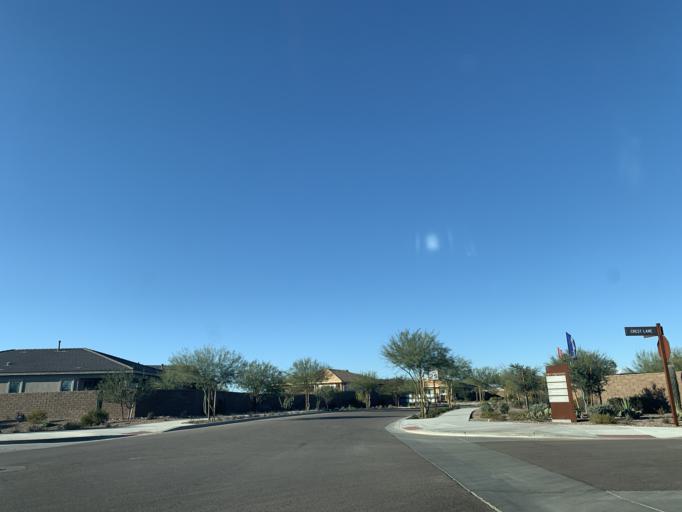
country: US
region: Arizona
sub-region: Maricopa County
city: Cave Creek
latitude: 33.6893
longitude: -112.0199
